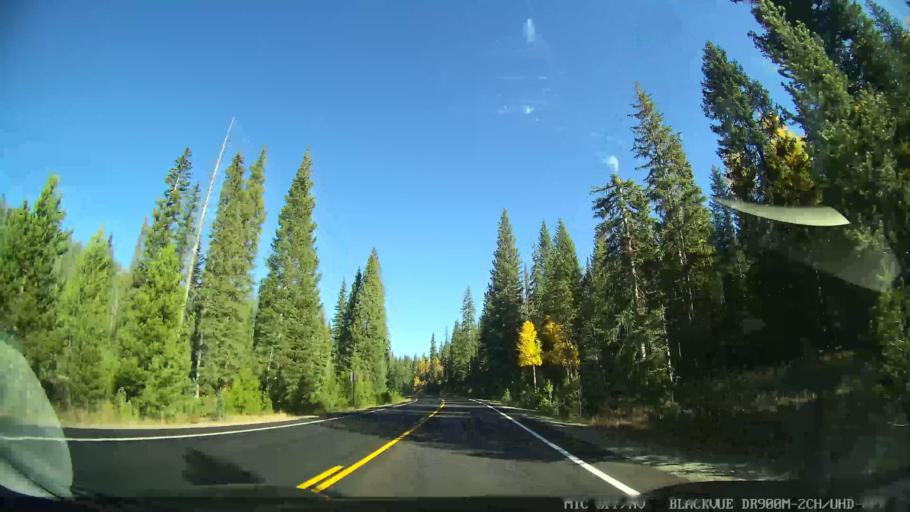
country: US
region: Colorado
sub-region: Grand County
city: Granby
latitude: 40.2975
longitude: -105.8427
